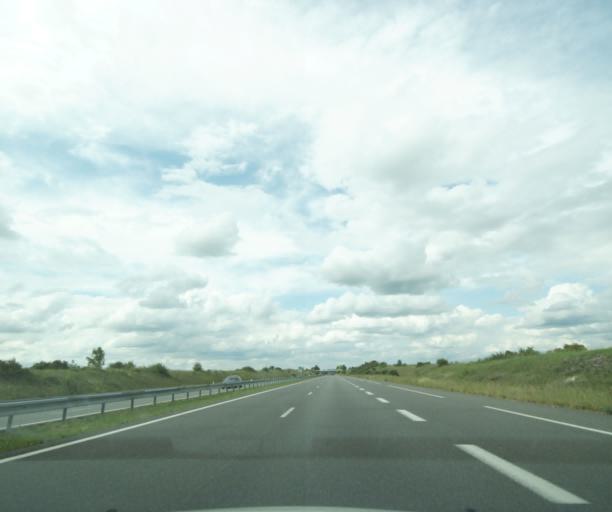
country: FR
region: Centre
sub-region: Departement du Cher
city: Mehun-sur-Yevre
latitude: 47.1490
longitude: 2.1850
